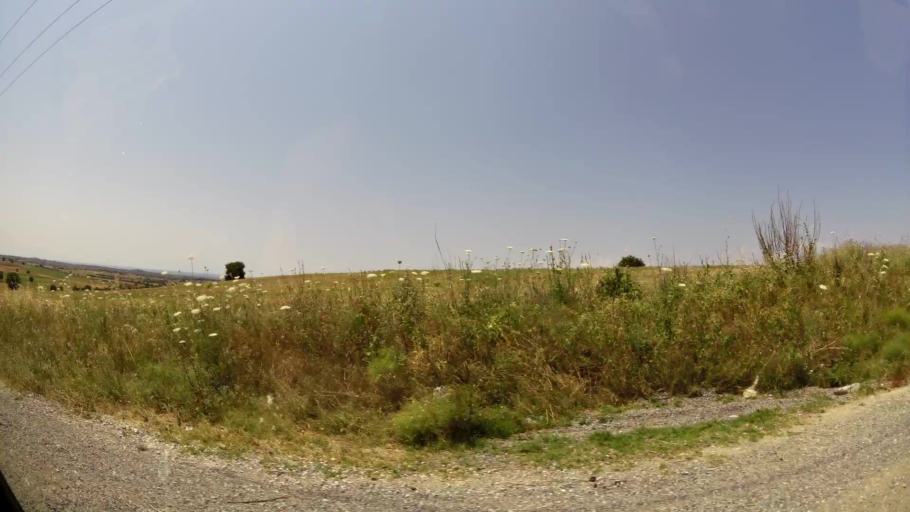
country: GR
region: Central Macedonia
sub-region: Nomos Thessalonikis
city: Neoi Epivates
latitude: 40.4659
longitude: 22.9021
